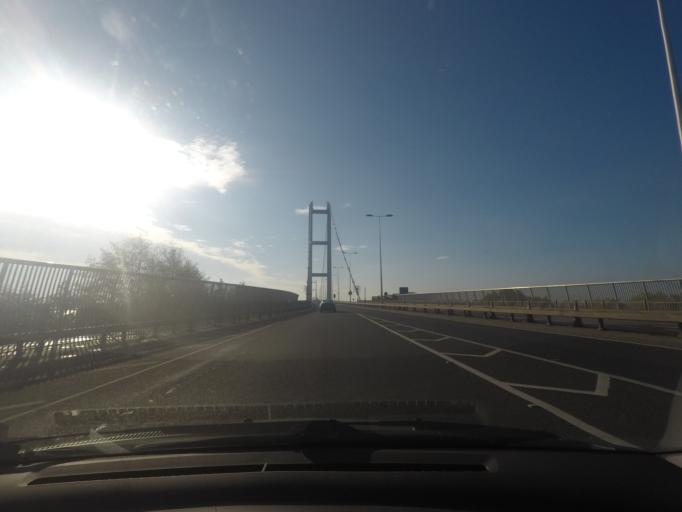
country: GB
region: England
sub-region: East Riding of Yorkshire
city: Hessle
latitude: 53.7182
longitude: -0.4508
